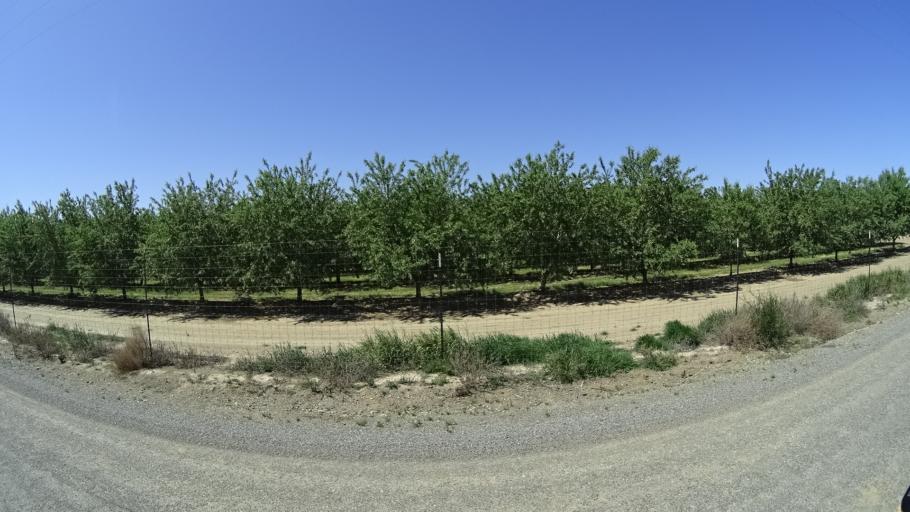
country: US
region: California
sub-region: Glenn County
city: Orland
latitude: 39.7934
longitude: -122.2300
